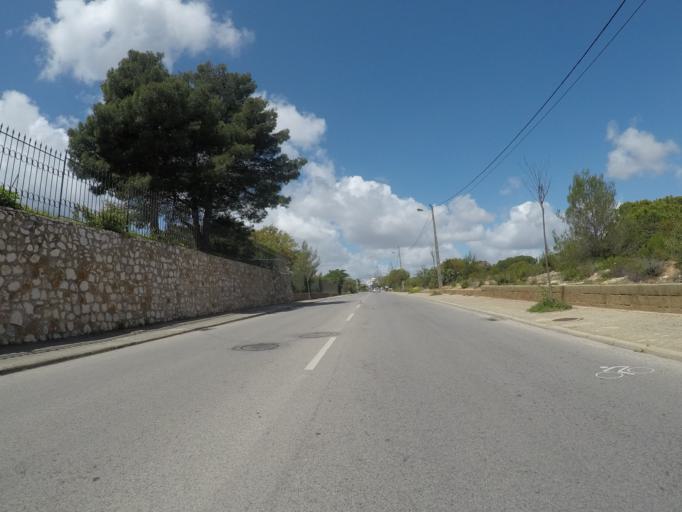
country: PT
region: Faro
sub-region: Silves
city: Armacao de Pera
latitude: 37.1052
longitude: -8.3774
